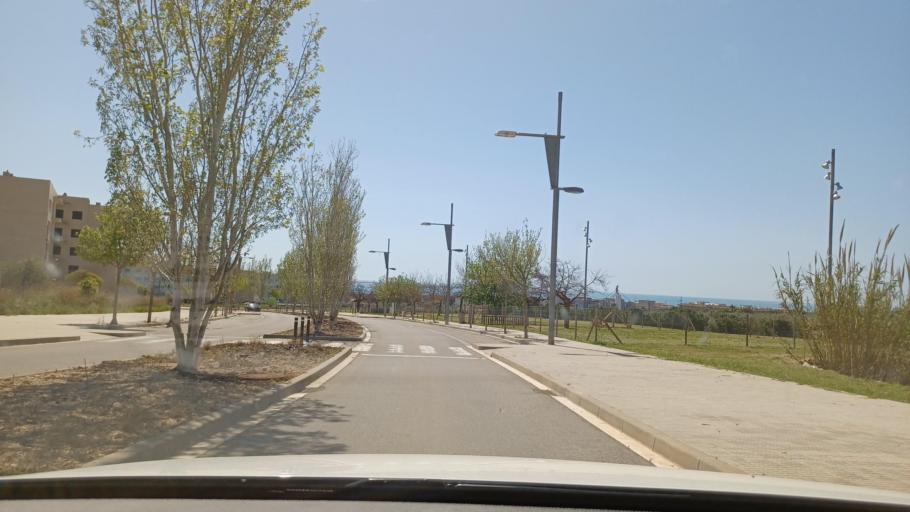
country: ES
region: Catalonia
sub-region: Provincia de Tarragona
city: Sant Carles de la Rapita
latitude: 40.6161
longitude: 0.5803
